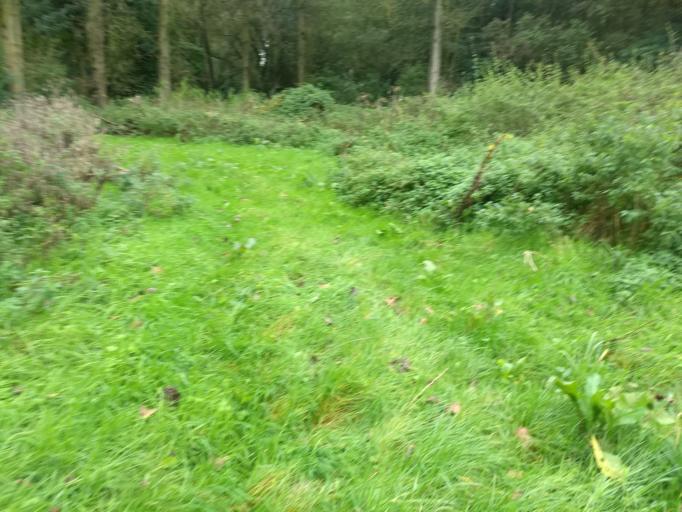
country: BE
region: Flanders
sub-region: Provincie Vlaams-Brabant
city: Sint-Pieters-Leeuw
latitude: 50.7884
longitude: 4.2236
